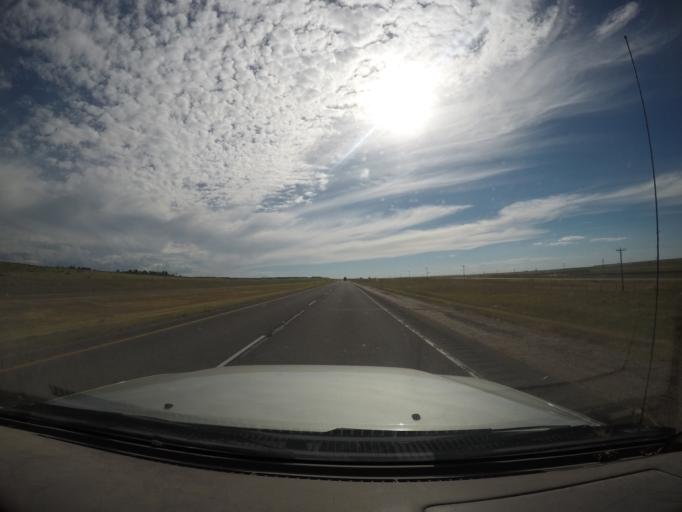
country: US
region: Wyoming
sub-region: Laramie County
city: Pine Bluffs
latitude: 41.1911
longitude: -103.9999
